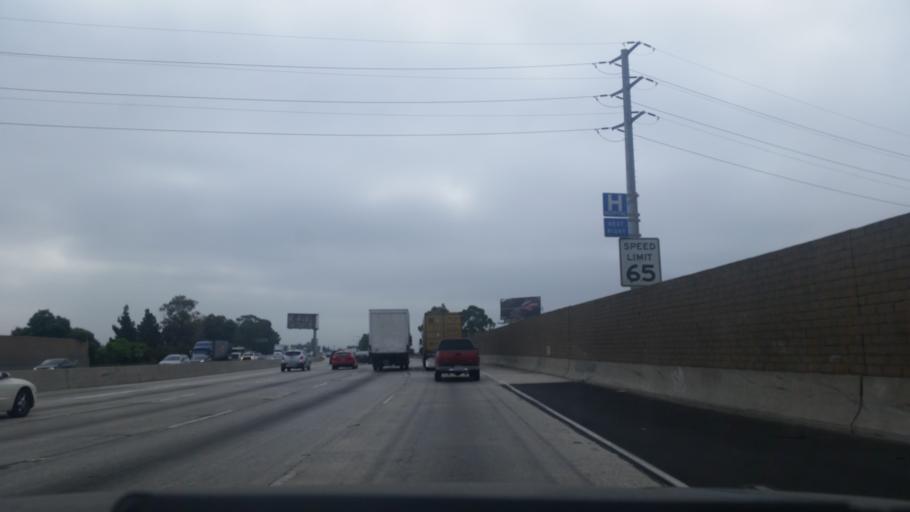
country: US
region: California
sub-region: Los Angeles County
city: Paramount
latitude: 33.8759
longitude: -118.1693
